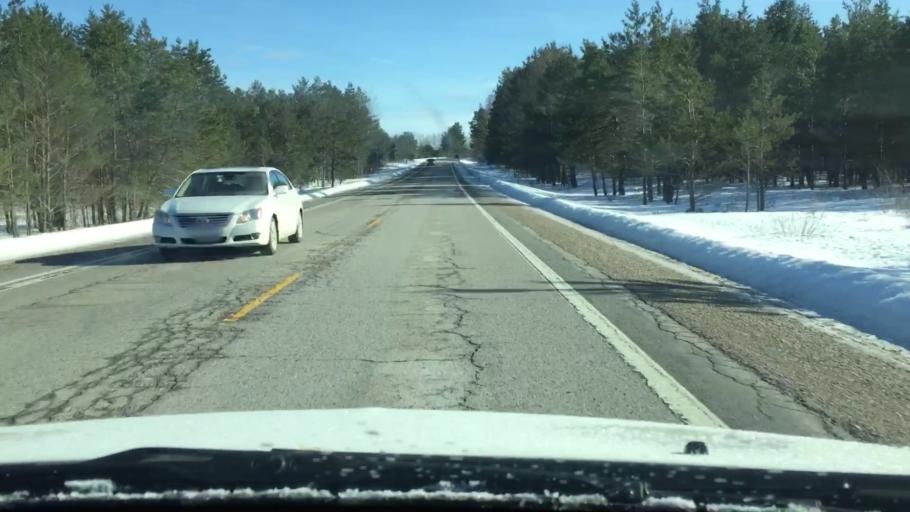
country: US
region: Michigan
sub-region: Charlevoix County
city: East Jordan
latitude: 45.0958
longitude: -85.1034
